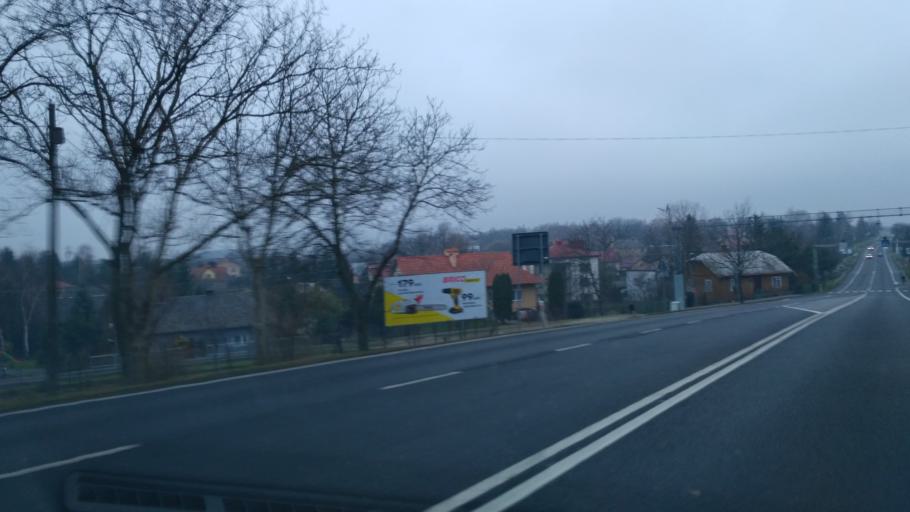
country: PL
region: Subcarpathian Voivodeship
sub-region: Powiat przeworski
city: Mirocin
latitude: 50.0416
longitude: 22.5578
